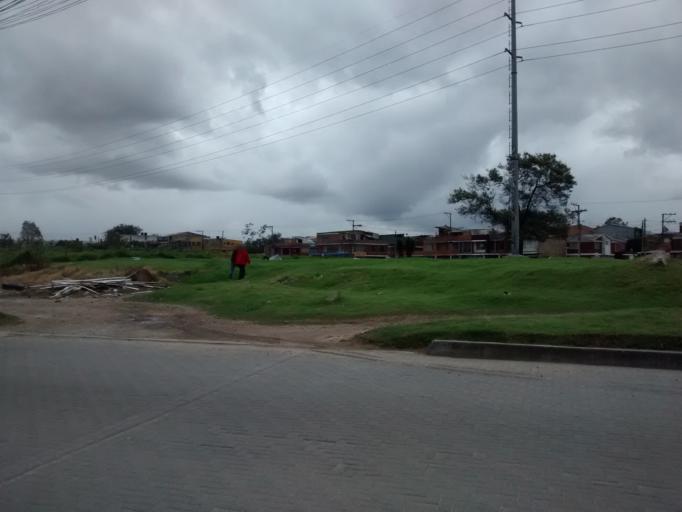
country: CO
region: Bogota D.C.
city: Bogota
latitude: 4.6975
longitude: -74.1162
